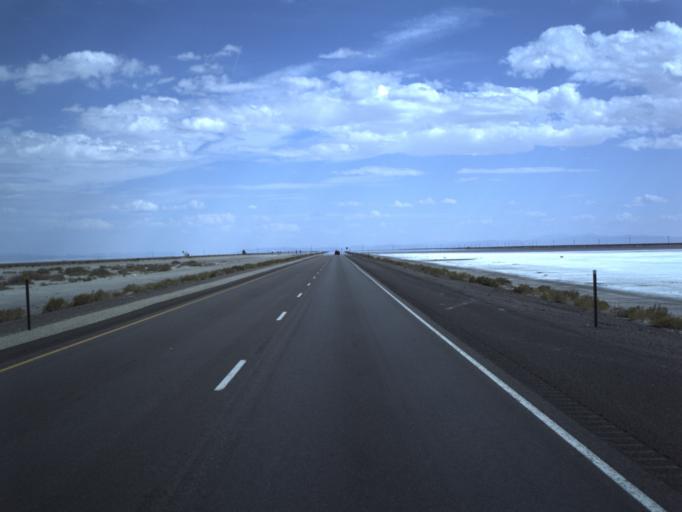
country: US
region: Utah
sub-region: Tooele County
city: Wendover
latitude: 40.7372
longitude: -113.7874
